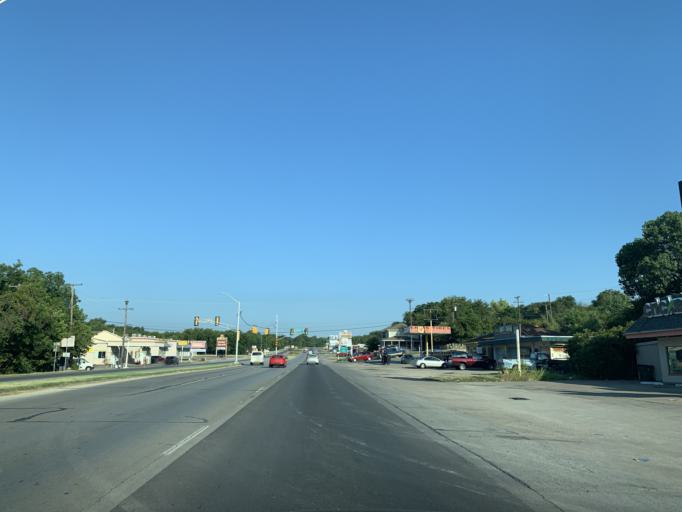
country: US
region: Texas
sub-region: Tarrant County
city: Sansom Park
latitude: 32.7957
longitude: -97.3972
